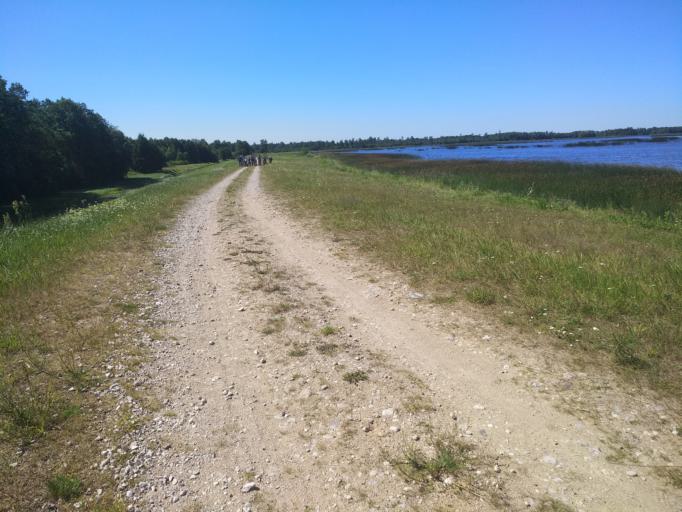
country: EE
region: Harju
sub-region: Anija vald
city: Kehra
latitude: 59.1064
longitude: 25.3715
